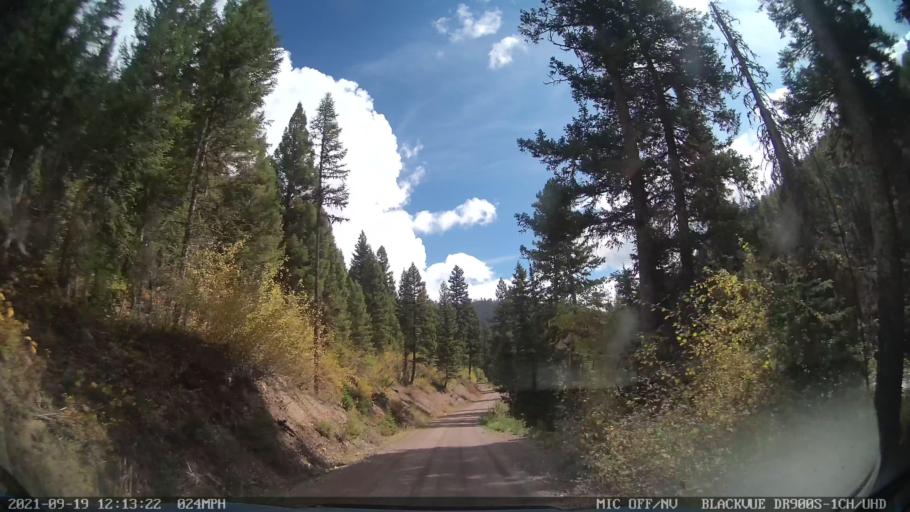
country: US
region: Montana
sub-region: Missoula County
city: Seeley Lake
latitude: 47.1682
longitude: -113.3580
